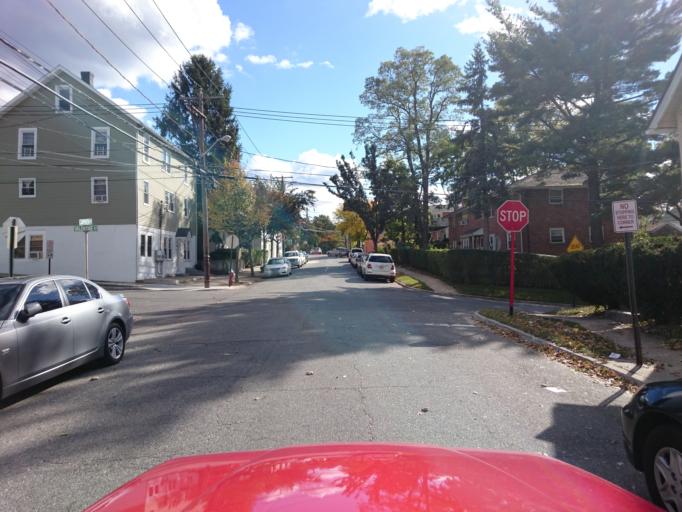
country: US
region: New York
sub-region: Nassau County
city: Glen Cove
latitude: 40.8653
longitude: -73.6463
